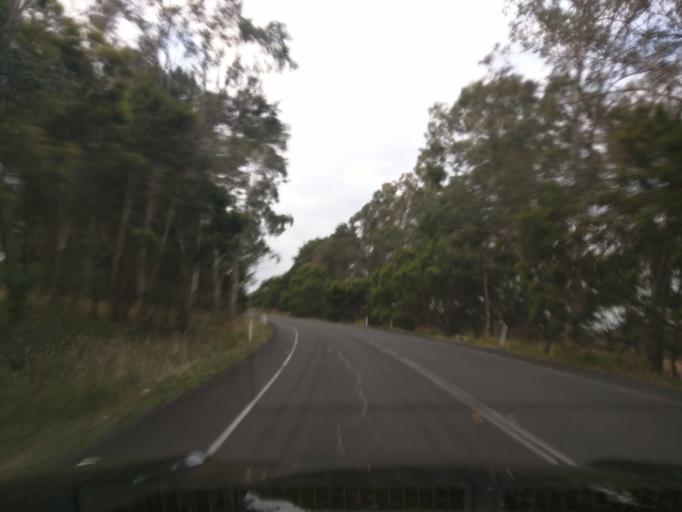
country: AU
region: New South Wales
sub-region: Wollondilly
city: Douglas Park
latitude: -34.2636
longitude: 150.7189
